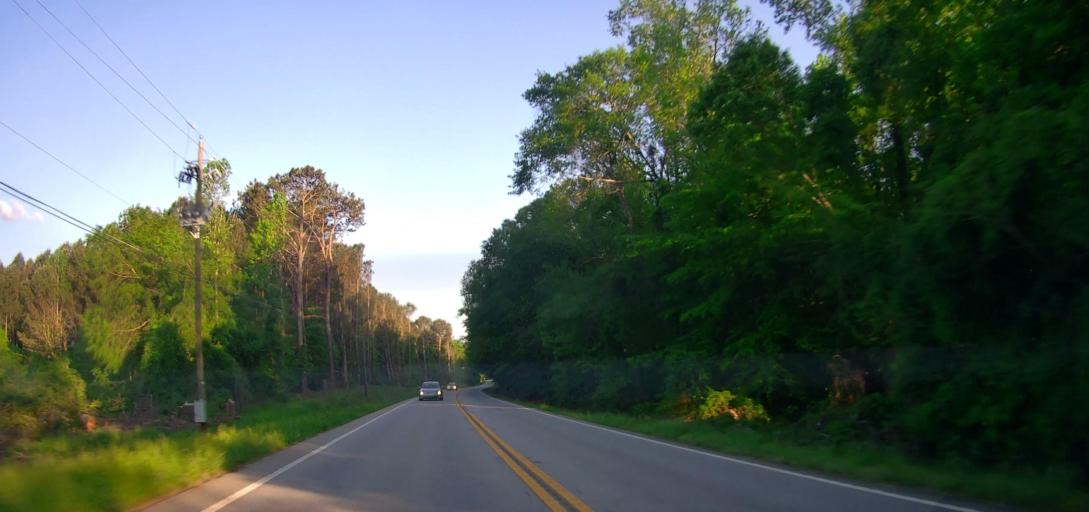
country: US
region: Georgia
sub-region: Walton County
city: Social Circle
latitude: 33.5446
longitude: -83.7291
